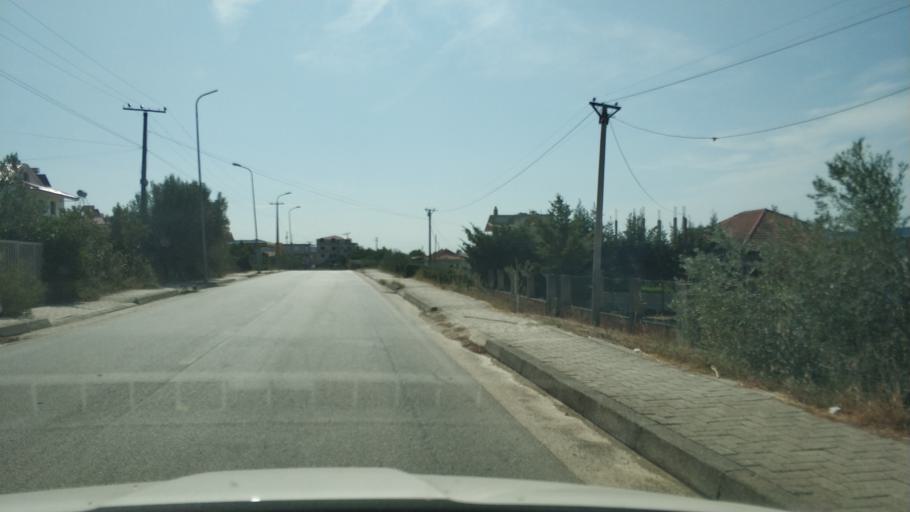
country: AL
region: Fier
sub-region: Rrethi i Lushnjes
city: Divjake
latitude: 40.9796
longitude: 19.5352
